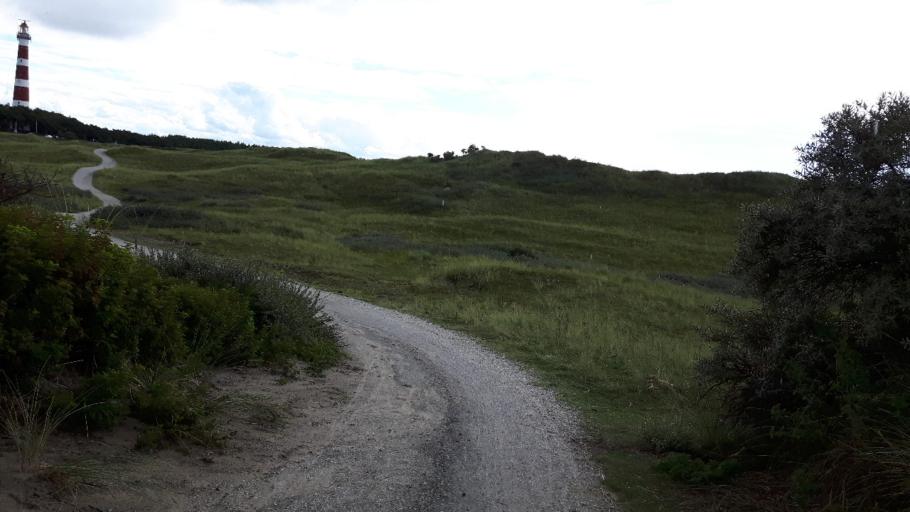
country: NL
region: Friesland
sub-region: Gemeente Ameland
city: Hollum
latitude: 53.4518
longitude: 5.6207
